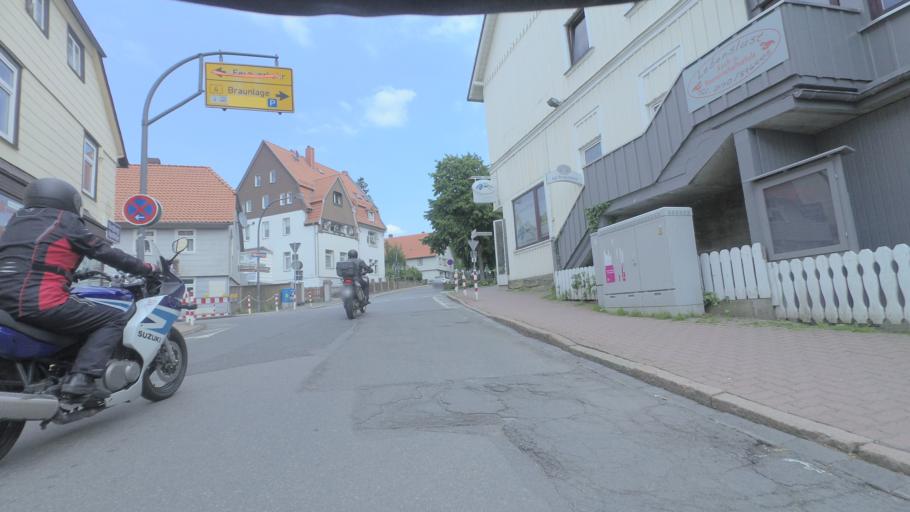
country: DE
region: Lower Saxony
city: Bad Harzburg
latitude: 51.8801
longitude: 10.5626
